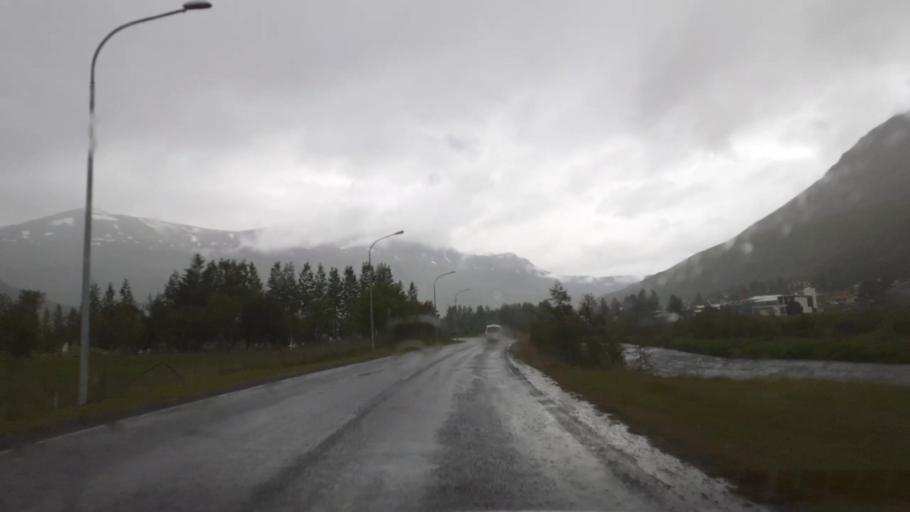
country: IS
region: East
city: Eskifjoerdur
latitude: 65.2538
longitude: -14.0153
